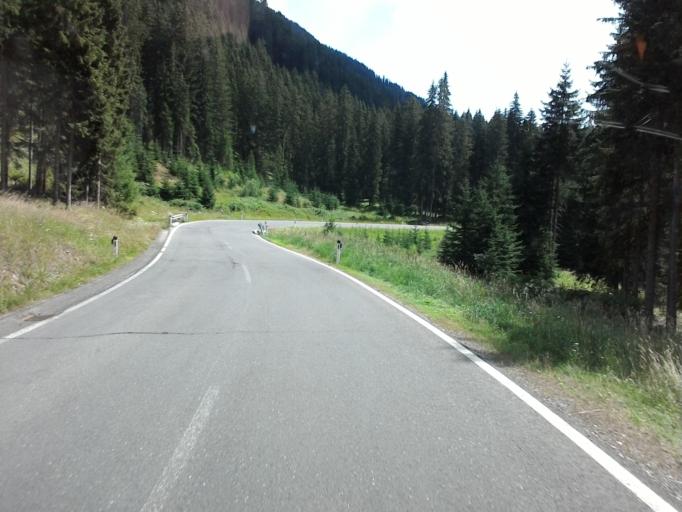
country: AT
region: Tyrol
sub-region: Politischer Bezirk Lienz
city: Obertilliach
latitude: 46.7138
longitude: 12.5757
